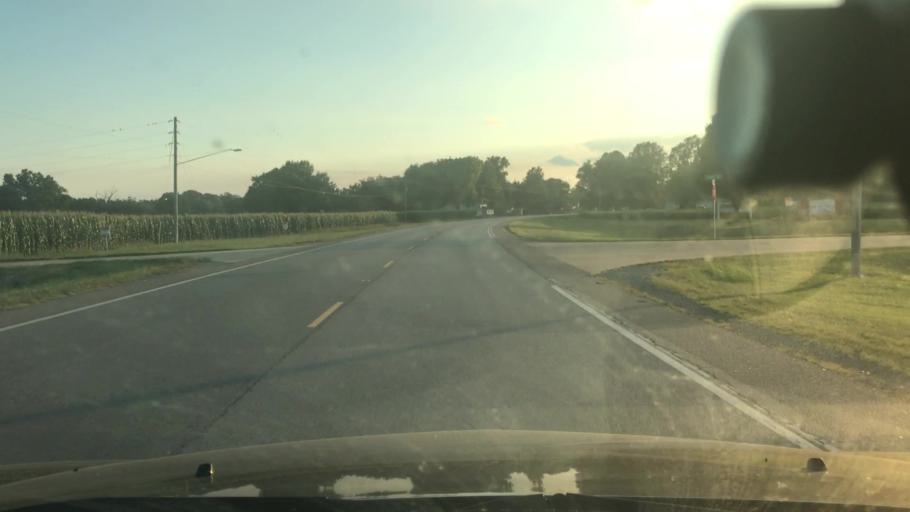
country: US
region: Illinois
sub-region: Washington County
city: Okawville
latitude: 38.4364
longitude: -89.5378
